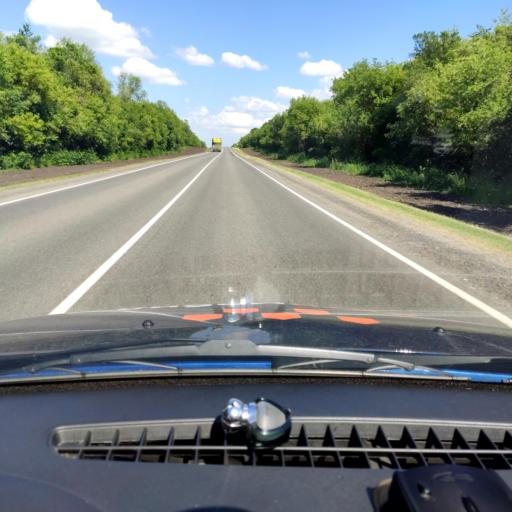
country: RU
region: Orjol
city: Livny
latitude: 52.4253
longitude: 37.7485
